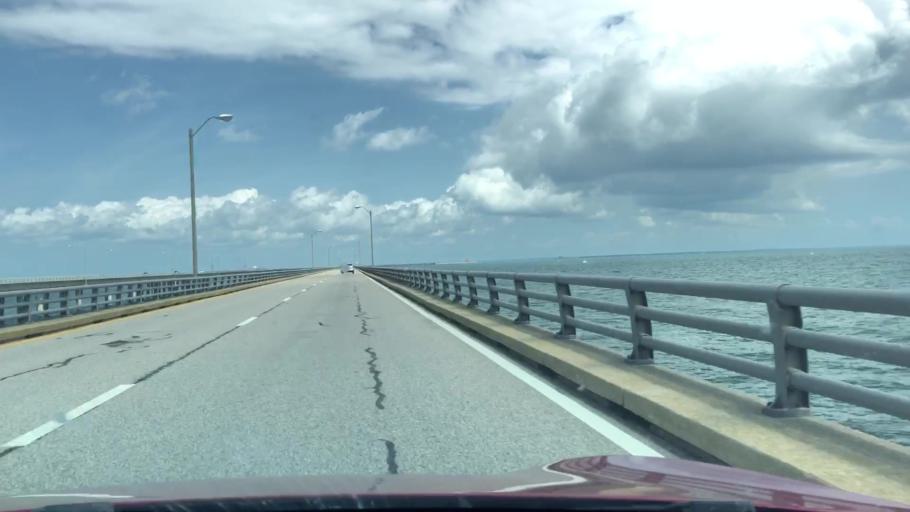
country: US
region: Virginia
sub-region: City of Virginia Beach
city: Virginia Beach
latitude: 37.0009
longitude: -76.0982
